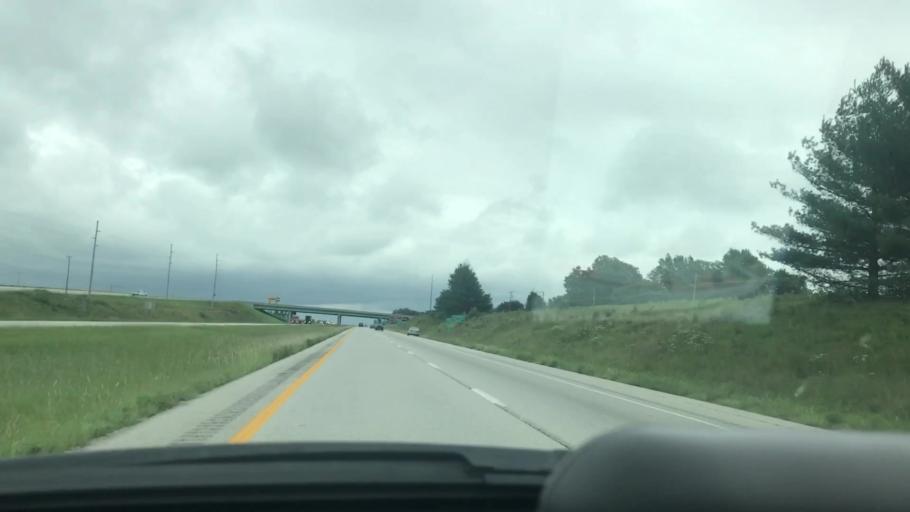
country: US
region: Missouri
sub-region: Jasper County
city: Duquesne
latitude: 37.0539
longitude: -94.4493
